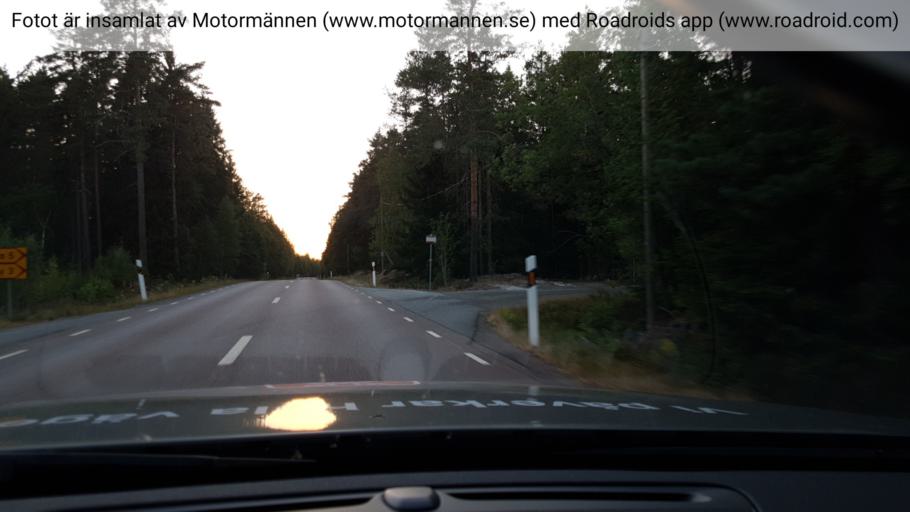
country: SE
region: Uppsala
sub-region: Heby Kommun
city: OEstervala
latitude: 60.0370
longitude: 17.2528
